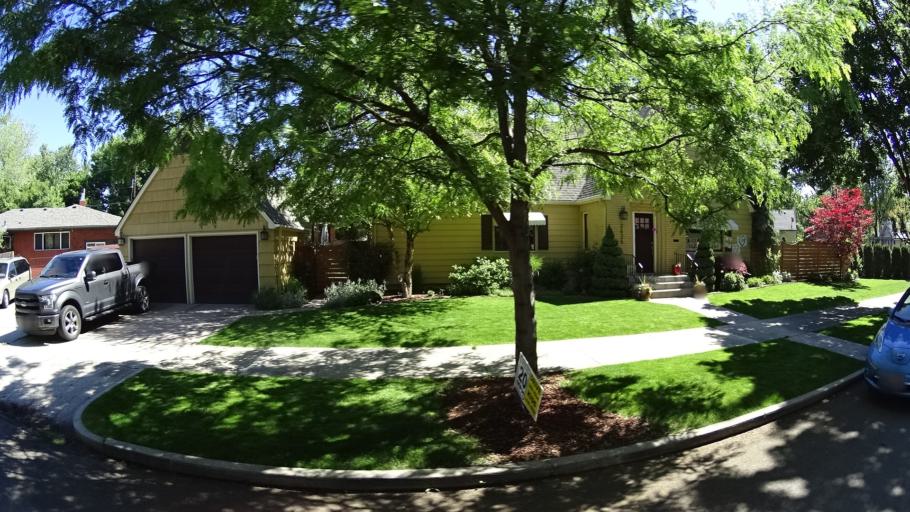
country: US
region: Idaho
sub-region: Ada County
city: Garden City
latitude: 43.6325
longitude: -116.2219
